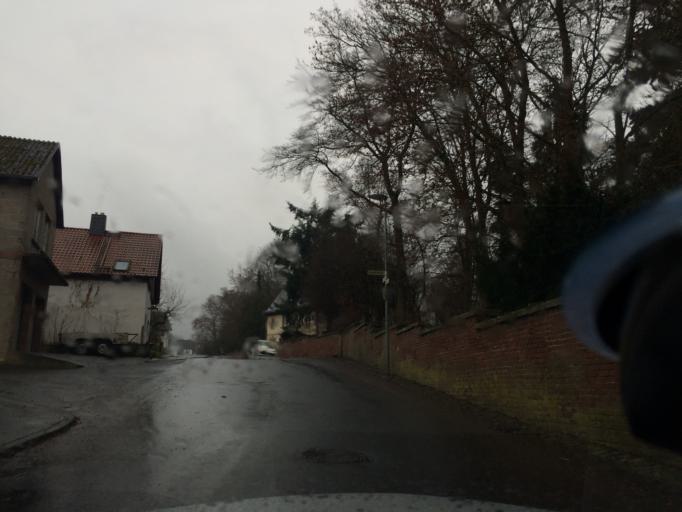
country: DE
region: Hesse
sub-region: Regierungsbezirk Giessen
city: Ebsdorfergrund
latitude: 50.7569
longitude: 8.8836
